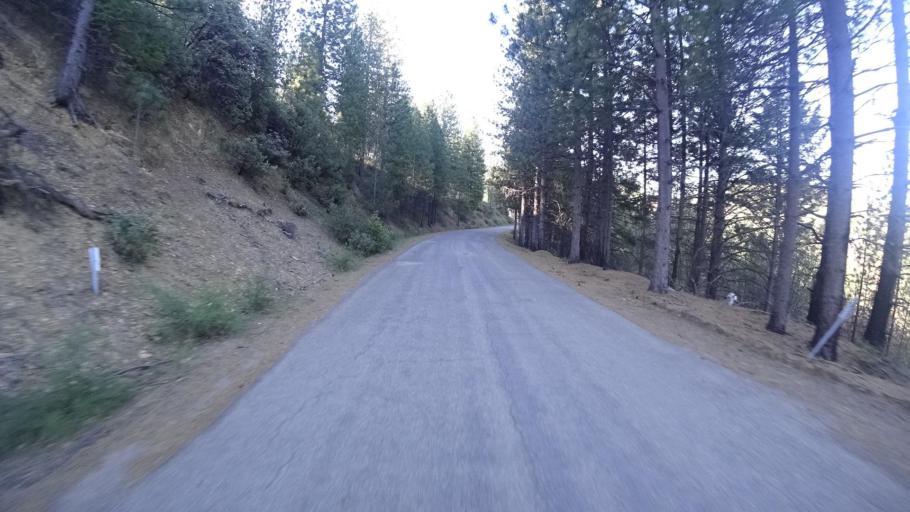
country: US
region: California
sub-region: Lake County
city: Upper Lake
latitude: 39.2888
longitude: -122.9264
